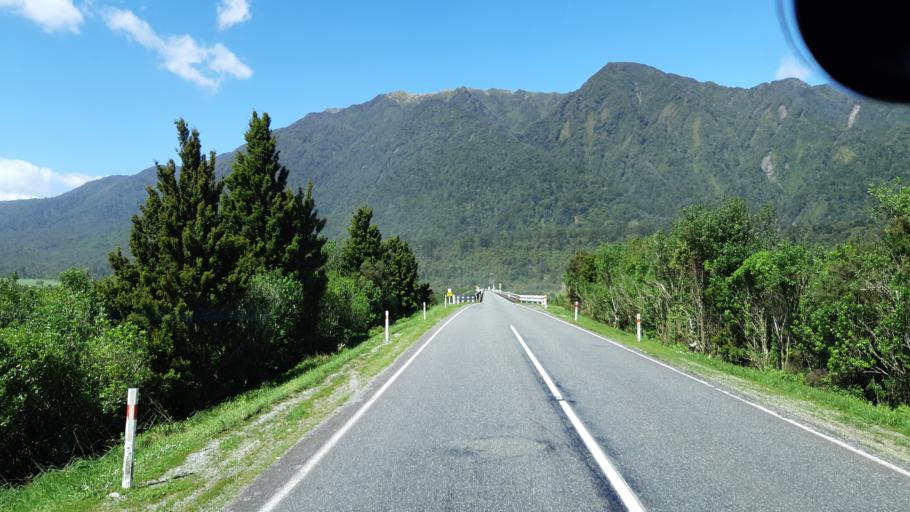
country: NZ
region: West Coast
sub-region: Westland District
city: Hokitika
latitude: -43.1556
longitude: 170.6201
